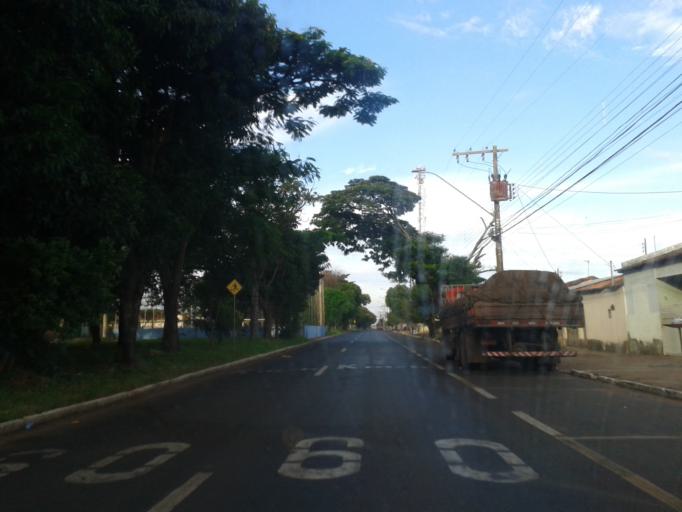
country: BR
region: Minas Gerais
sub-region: Araguari
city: Araguari
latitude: -18.6408
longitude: -48.2080
